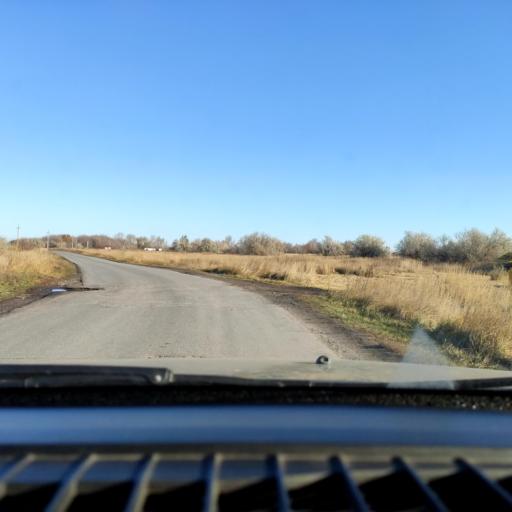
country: RU
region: Samara
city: Tol'yatti
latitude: 53.6561
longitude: 49.3311
